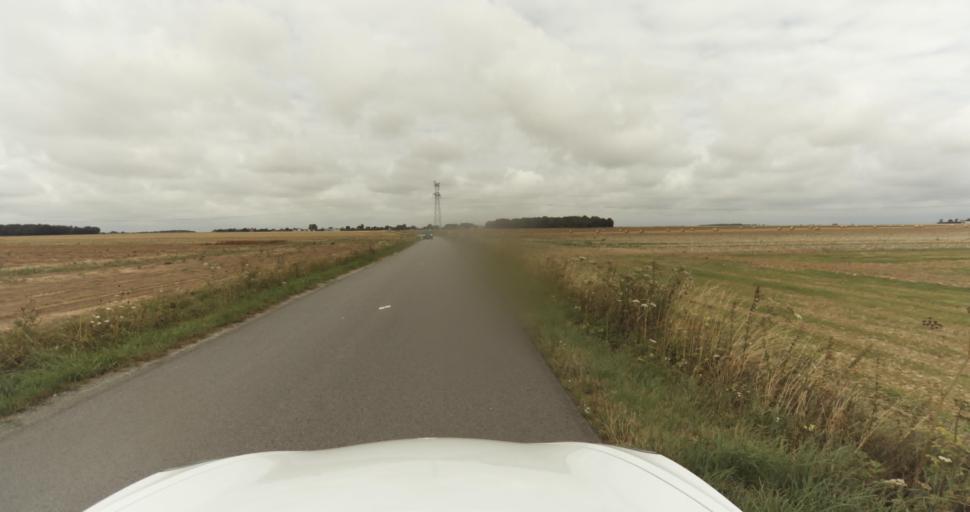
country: FR
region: Haute-Normandie
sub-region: Departement de l'Eure
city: Claville
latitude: 49.0338
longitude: 1.0295
